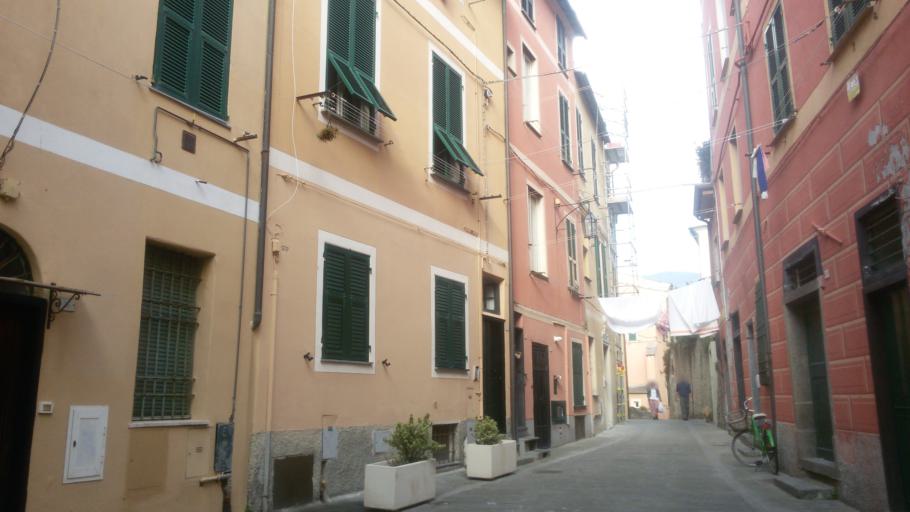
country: IT
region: Liguria
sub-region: Provincia di La Spezia
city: Levanto
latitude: 44.1687
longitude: 9.6122
